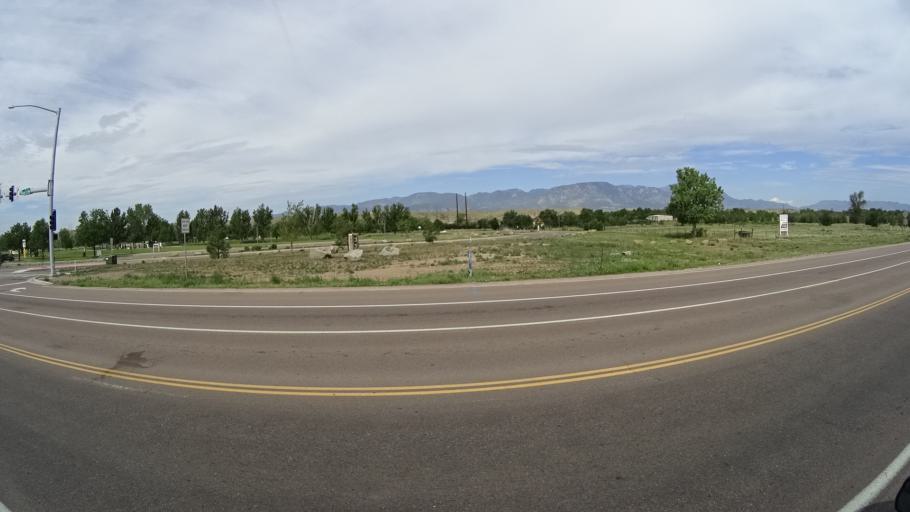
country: US
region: Colorado
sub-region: El Paso County
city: Fountain
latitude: 38.7100
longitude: -104.7119
